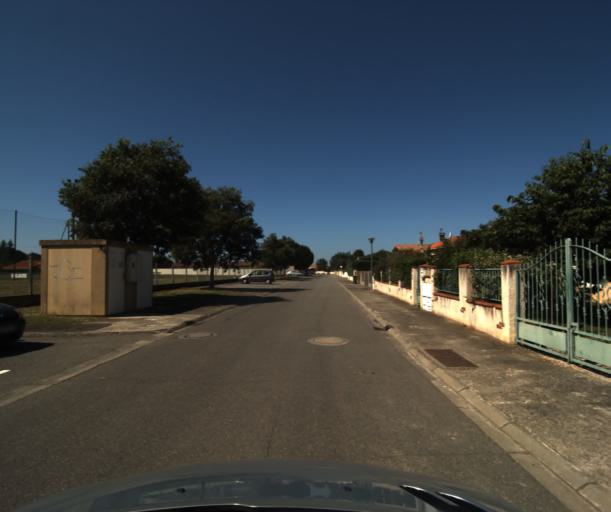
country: FR
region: Midi-Pyrenees
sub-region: Departement de la Haute-Garonne
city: Roquettes
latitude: 43.5007
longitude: 1.3733
